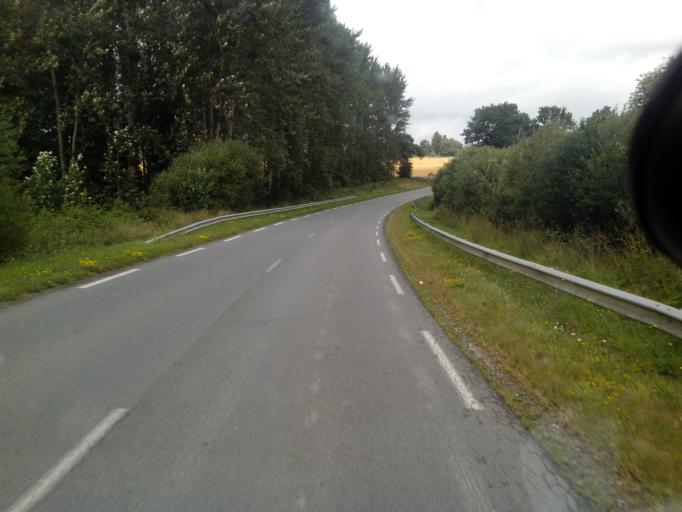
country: FR
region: Brittany
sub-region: Departement des Cotes-d'Armor
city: Merdrignac
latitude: 48.1814
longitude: -2.4299
